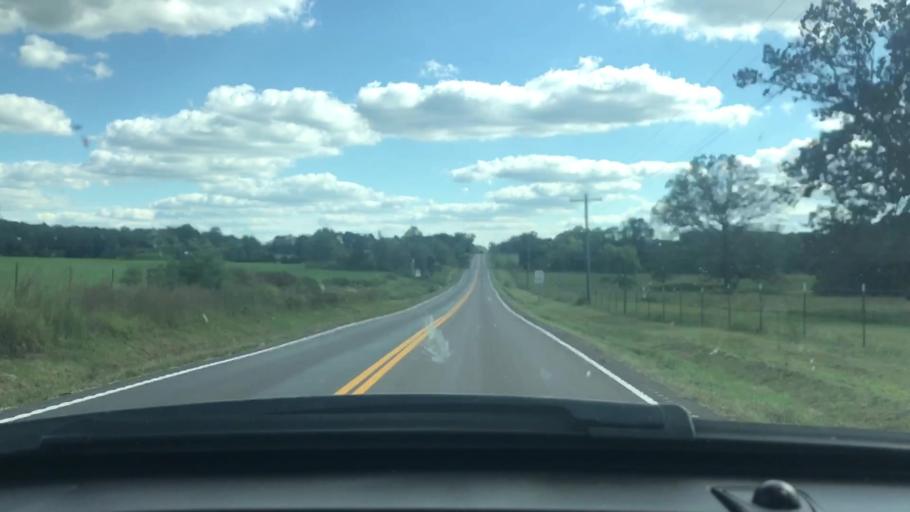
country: US
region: Missouri
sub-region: Wright County
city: Mountain Grove
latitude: 37.2419
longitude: -92.3004
